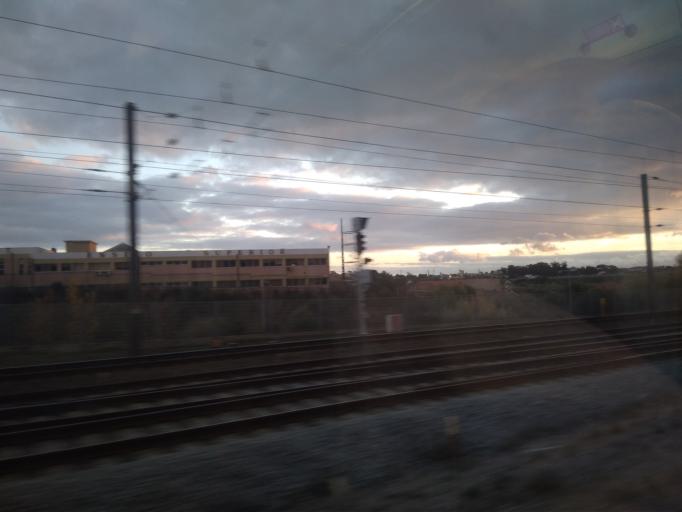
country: PT
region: Setubal
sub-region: Almada
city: Pragal
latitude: 38.6673
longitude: -9.1771
